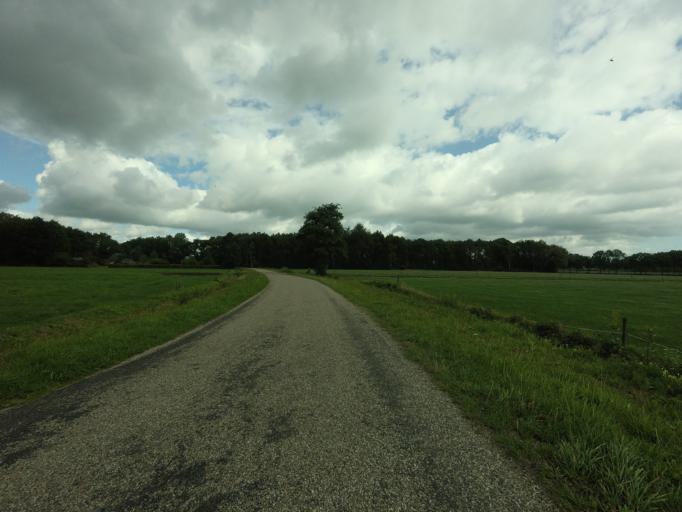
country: NL
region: Friesland
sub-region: Gemeente Heerenveen
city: Jubbega
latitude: 52.9811
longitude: 6.2787
